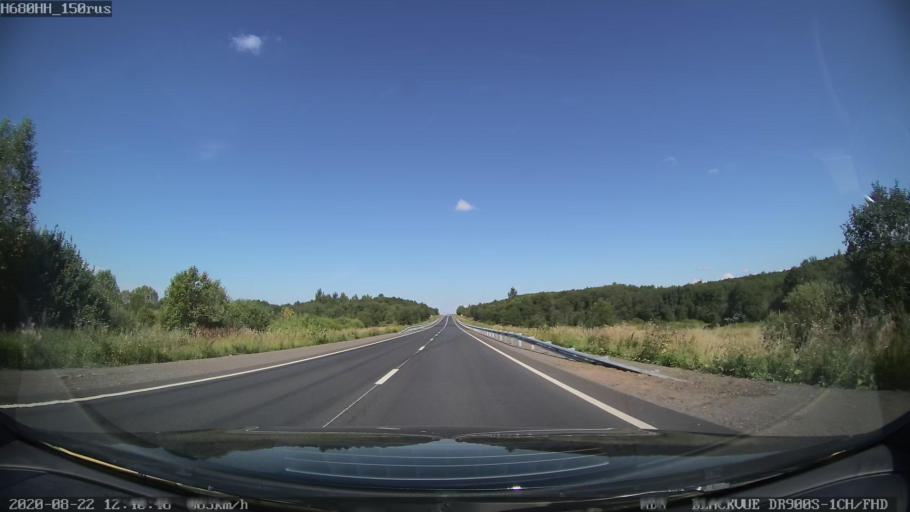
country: RU
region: Tverskaya
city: Rameshki
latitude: 57.3383
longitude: 36.0956
